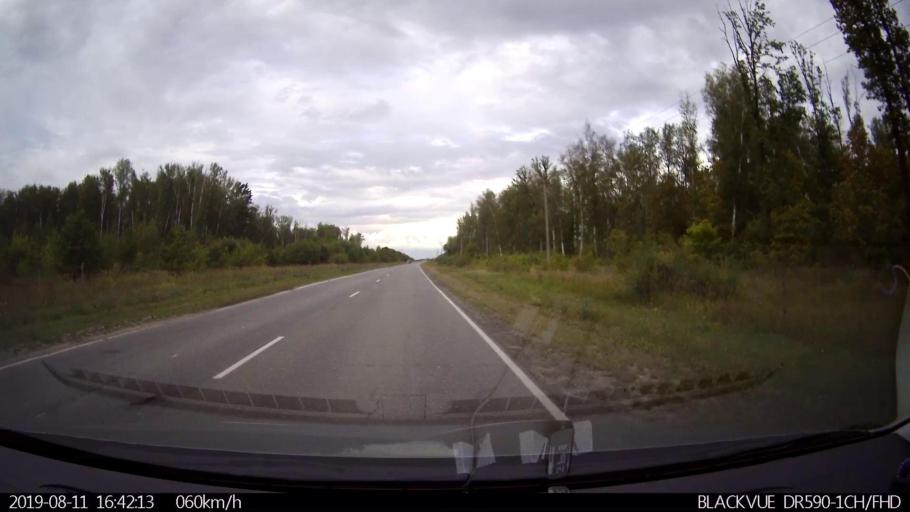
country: RU
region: Ulyanovsk
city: Mayna
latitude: 54.1588
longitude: 47.6604
